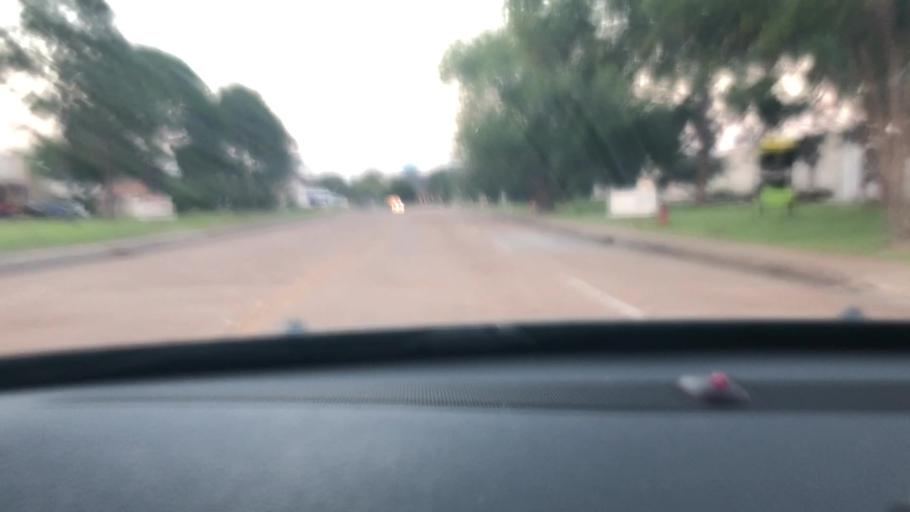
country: US
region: Texas
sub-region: Harris County
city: Webster
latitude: 29.5510
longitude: -95.1197
